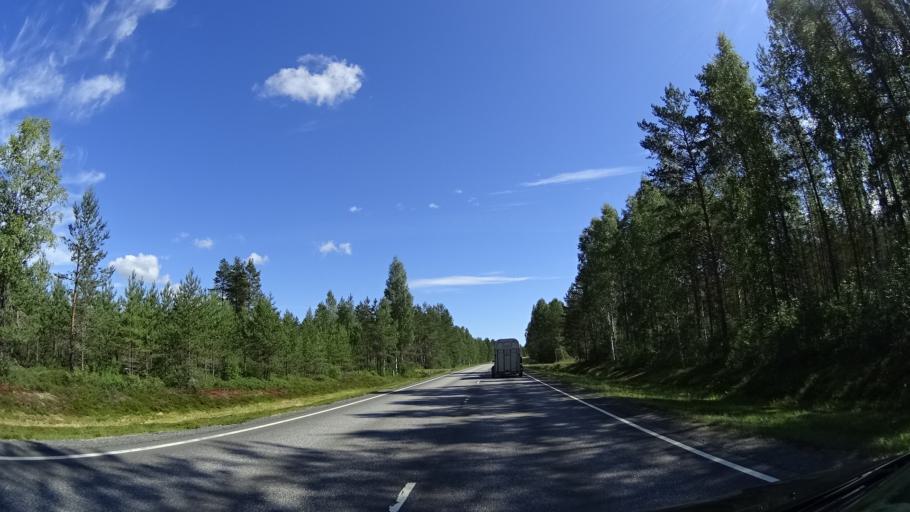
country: FI
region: Pirkanmaa
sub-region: Luoteis-Pirkanmaa
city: Kihnioe
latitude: 62.2305
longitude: 23.2986
